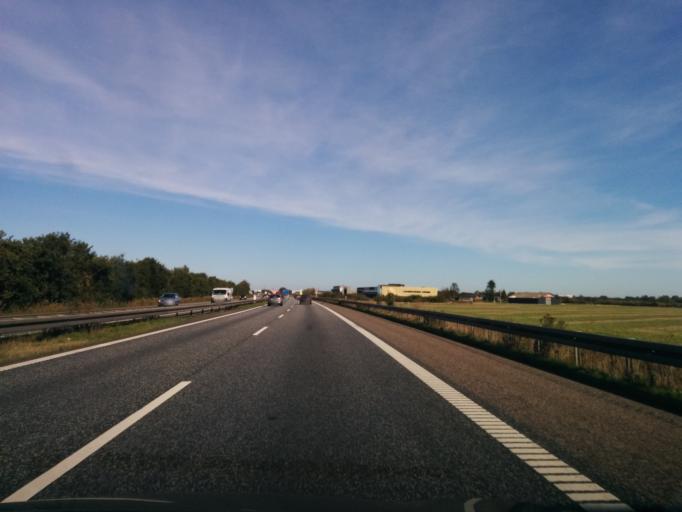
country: DK
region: Central Jutland
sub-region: Hedensted Kommune
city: Hedensted
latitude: 55.7790
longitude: 9.6589
